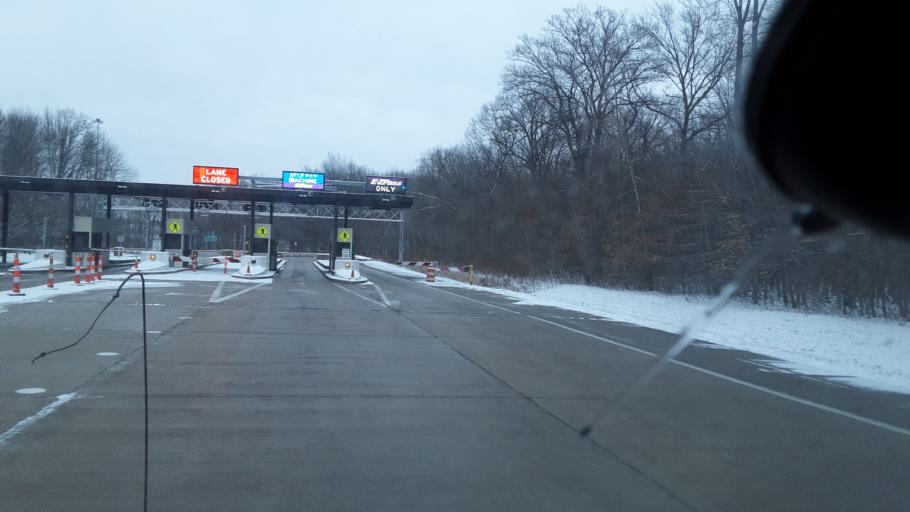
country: US
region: Ohio
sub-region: Trumbull County
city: Lordstown
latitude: 41.1397
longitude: -80.8675
